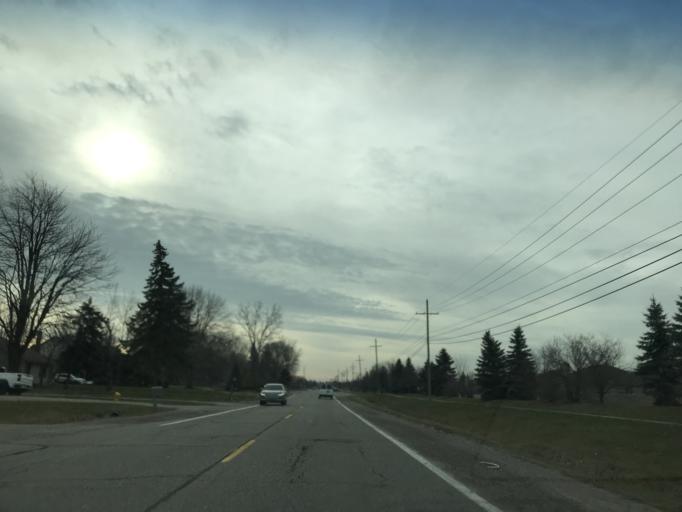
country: US
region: Michigan
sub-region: Macomb County
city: Mount Clemens
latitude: 42.6477
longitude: -82.8969
